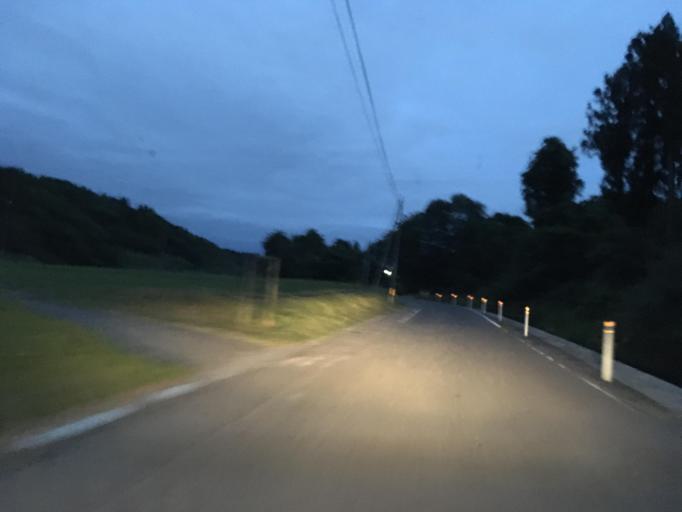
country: JP
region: Miyagi
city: Furukawa
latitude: 38.7865
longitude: 140.9385
